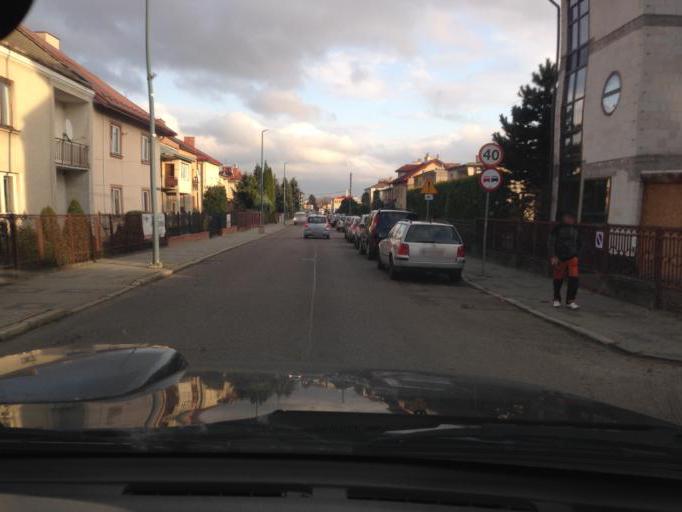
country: PL
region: Subcarpathian Voivodeship
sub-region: Powiat jasielski
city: Jaslo
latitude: 49.7463
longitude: 21.4771
